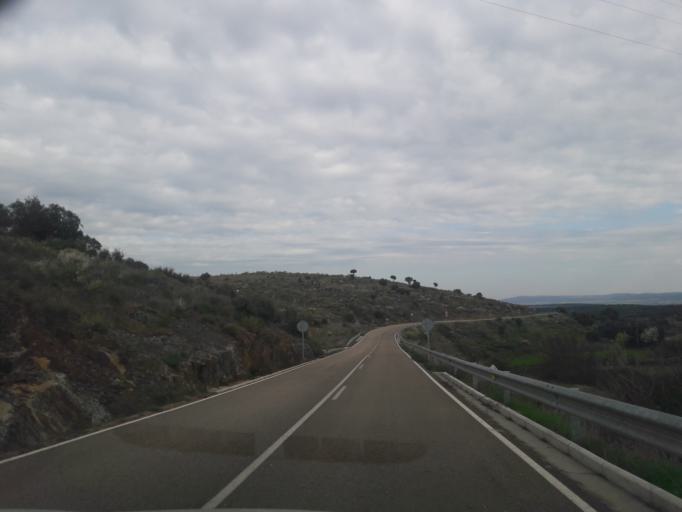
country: ES
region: Castille and Leon
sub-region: Provincia de Salamanca
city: Pastores
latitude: 40.5137
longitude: -6.5132
